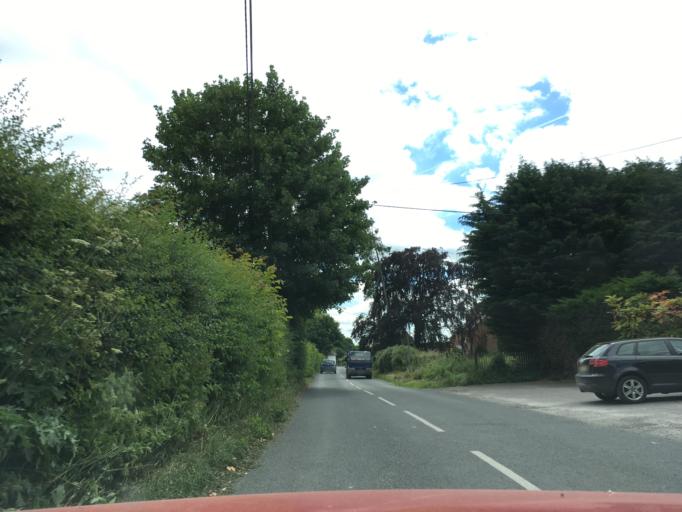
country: GB
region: England
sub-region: Hampshire
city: Highclere
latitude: 51.2469
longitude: -1.3916
